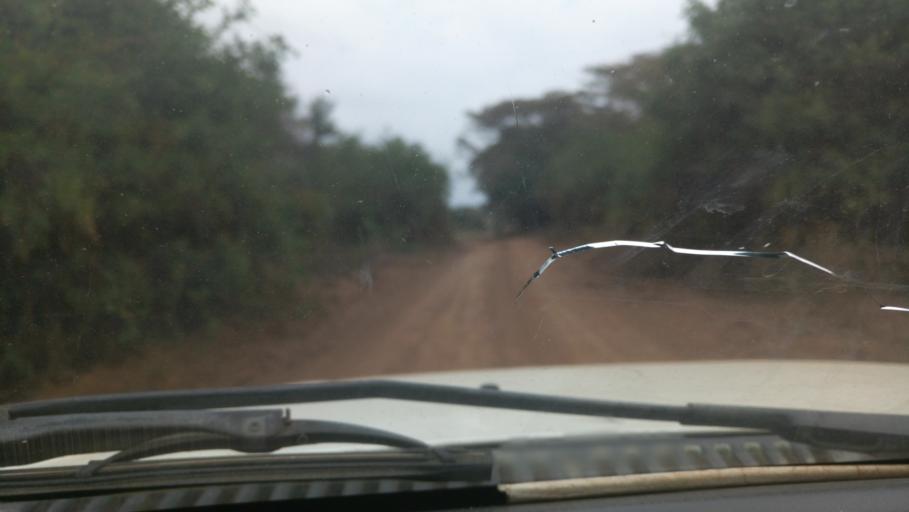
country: KE
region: Nairobi Area
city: Nairobi
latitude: -1.3765
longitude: 36.7810
